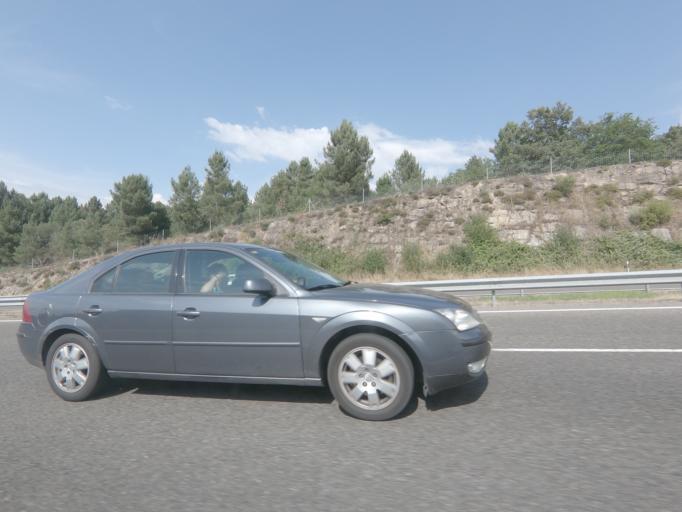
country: ES
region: Galicia
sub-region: Provincia de Ourense
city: Taboadela
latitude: 42.2735
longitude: -7.8722
